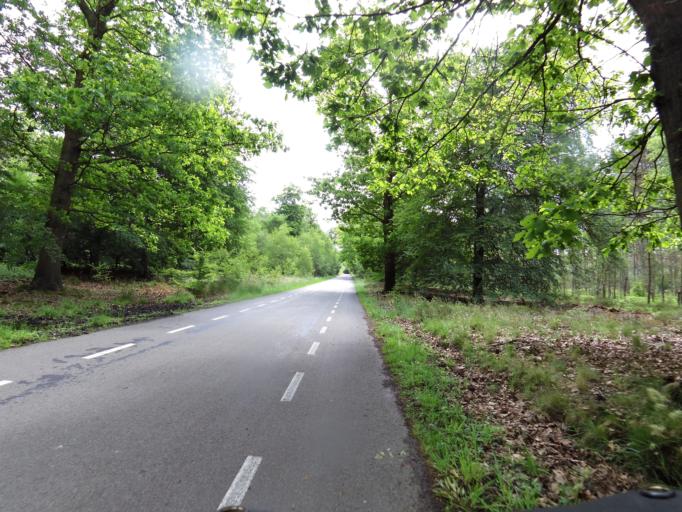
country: NL
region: Gelderland
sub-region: Gemeente Epe
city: Vaassen
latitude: 52.3034
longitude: 5.9037
